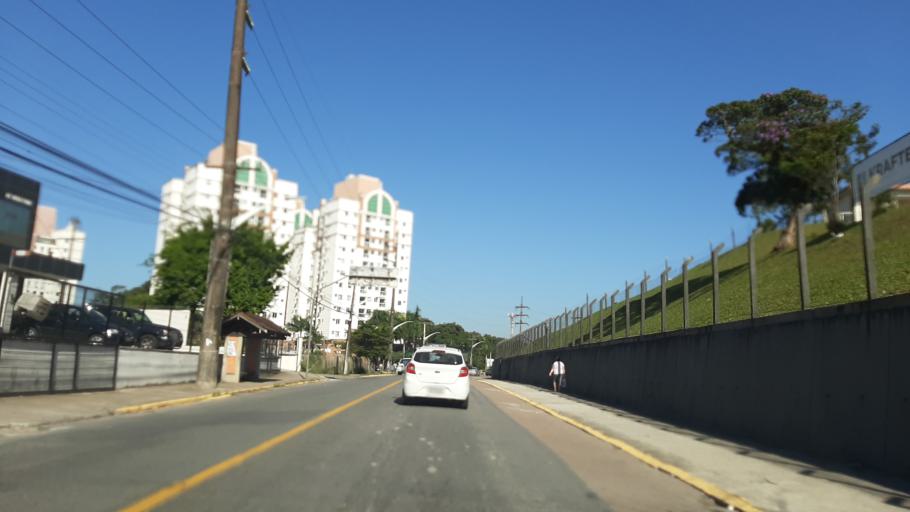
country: BR
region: Santa Catarina
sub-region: Joinville
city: Joinville
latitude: -26.3177
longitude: -48.8644
